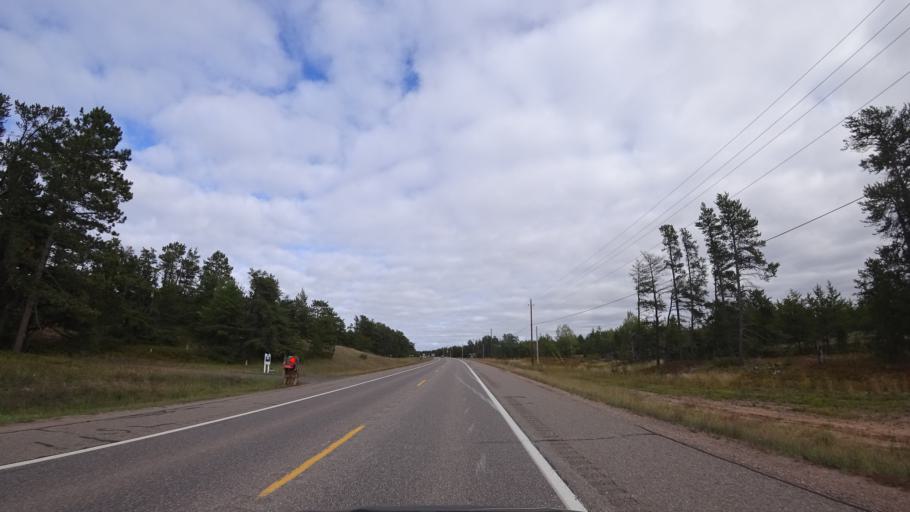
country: US
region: Michigan
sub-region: Marquette County
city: Harvey
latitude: 46.4850
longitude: -87.2542
